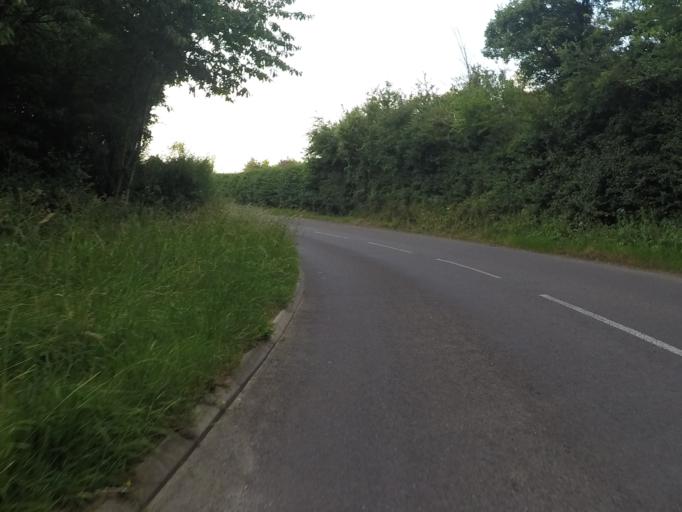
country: GB
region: England
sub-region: Oxfordshire
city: Charlbury
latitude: 51.8796
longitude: -1.4865
